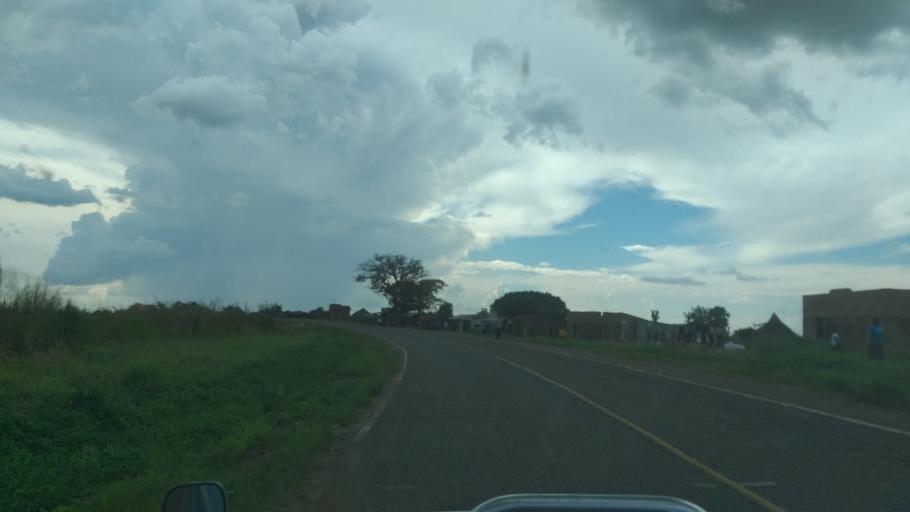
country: UG
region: Northern Region
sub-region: Nwoya District
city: Nwoya
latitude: 2.5798
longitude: 31.7732
